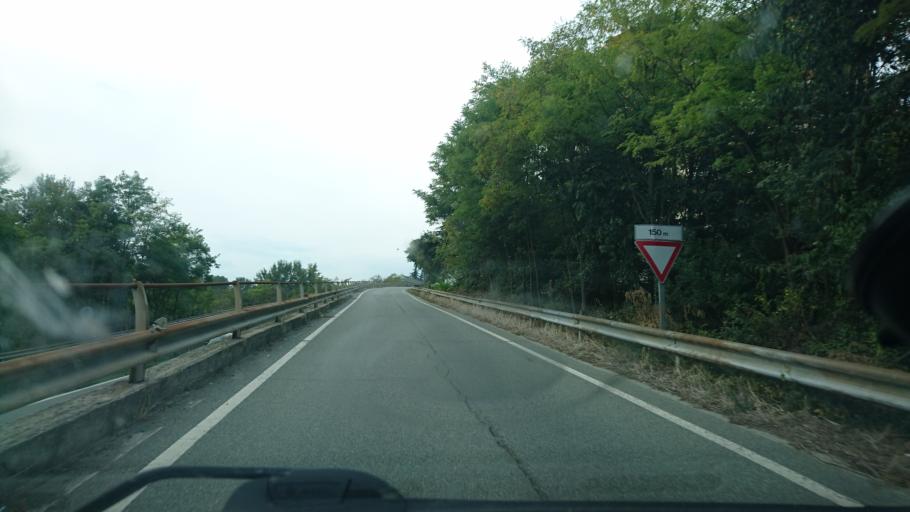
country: IT
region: Piedmont
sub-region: Provincia di Alessandria
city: Acqui Terme
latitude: 44.6668
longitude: 8.4723
